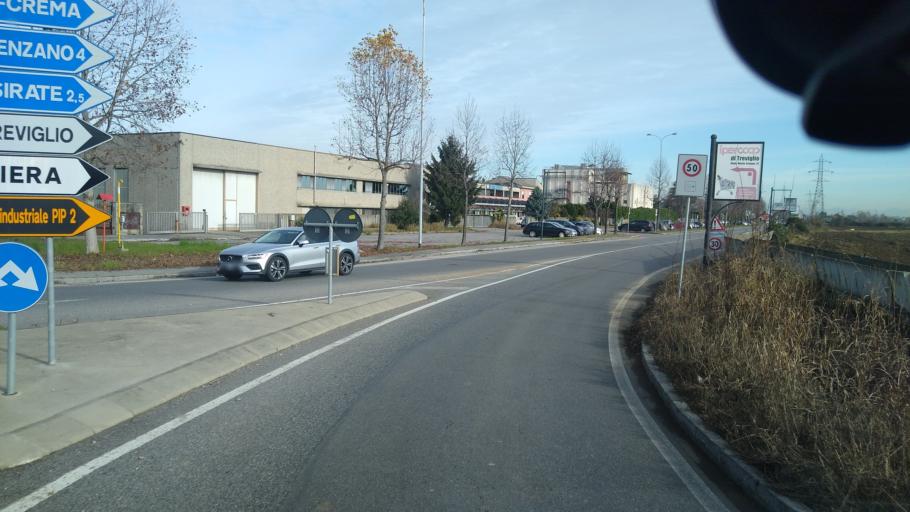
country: IT
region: Lombardy
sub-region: Provincia di Bergamo
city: Casirate d'Adda
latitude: 45.5075
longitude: 9.5682
